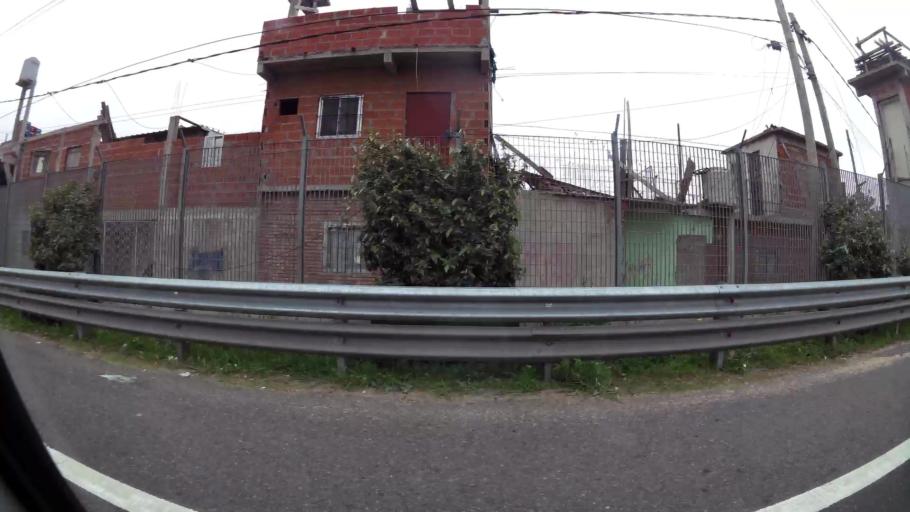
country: AR
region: Buenos Aires F.D.
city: Retiro
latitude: -34.5792
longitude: -58.3883
